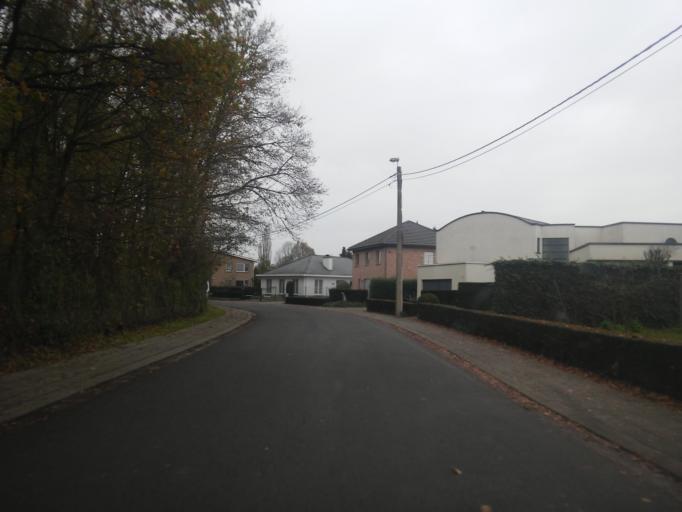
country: BE
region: Flanders
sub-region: Provincie Antwerpen
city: Bornem
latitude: 51.0901
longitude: 4.2480
